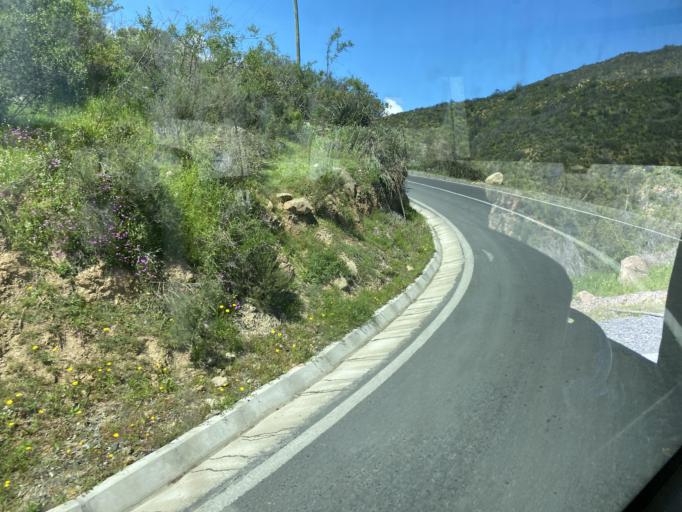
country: CL
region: Valparaiso
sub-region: Provincia de Marga Marga
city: Limache
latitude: -33.1969
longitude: -71.2725
